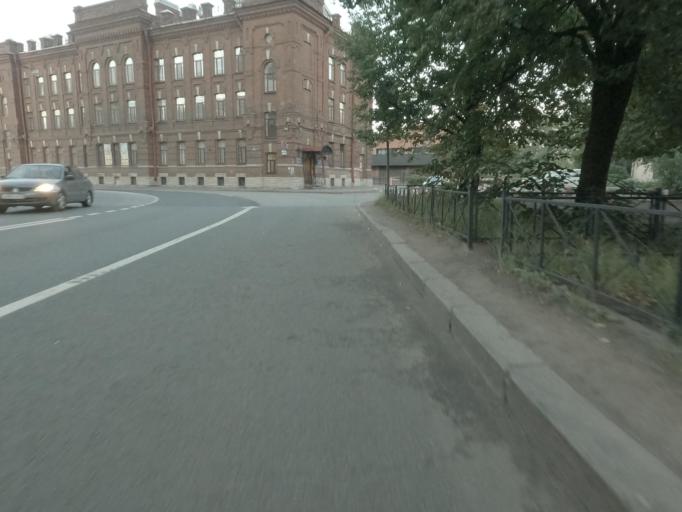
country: RU
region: St.-Petersburg
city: Admiralteisky
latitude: 59.9110
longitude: 30.2577
